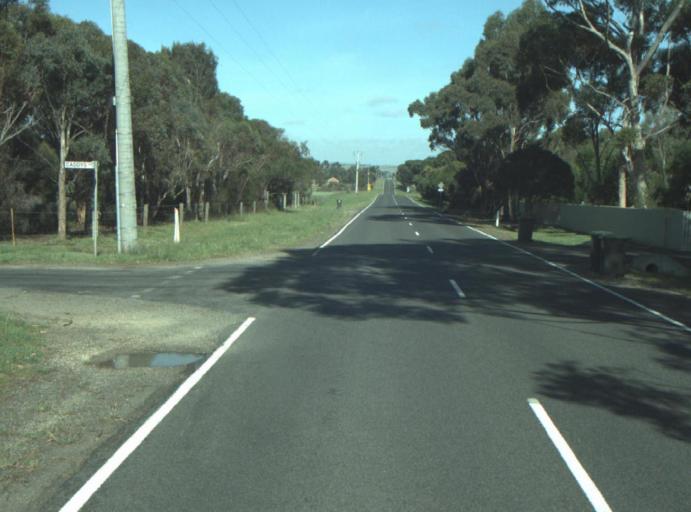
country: AU
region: Victoria
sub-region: Greater Geelong
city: Lara
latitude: -38.0100
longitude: 144.4106
